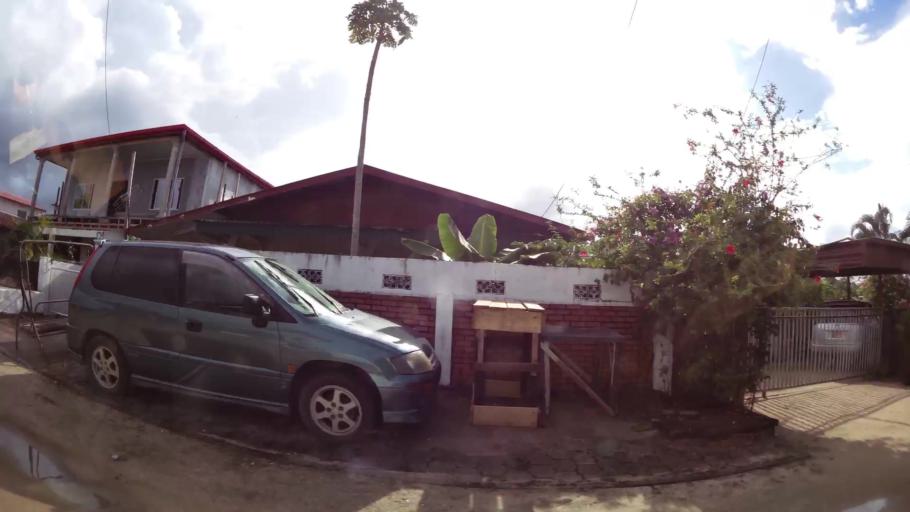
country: SR
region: Paramaribo
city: Paramaribo
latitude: 5.8460
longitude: -55.2123
